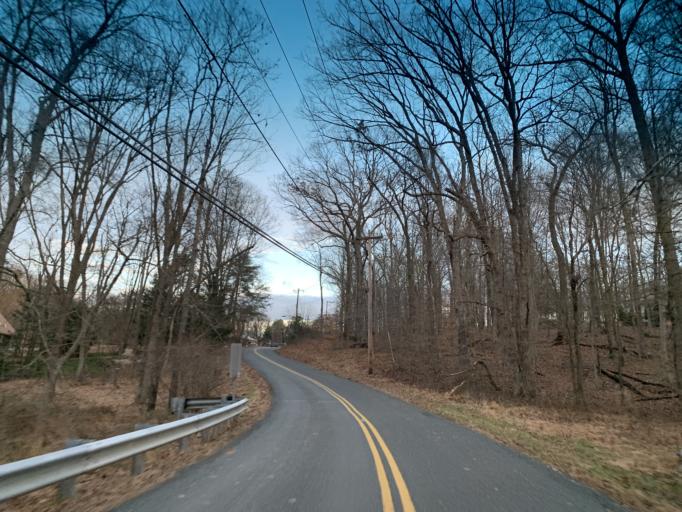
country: US
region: Pennsylvania
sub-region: York County
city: Susquehanna Trails
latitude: 39.6561
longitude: -76.3011
